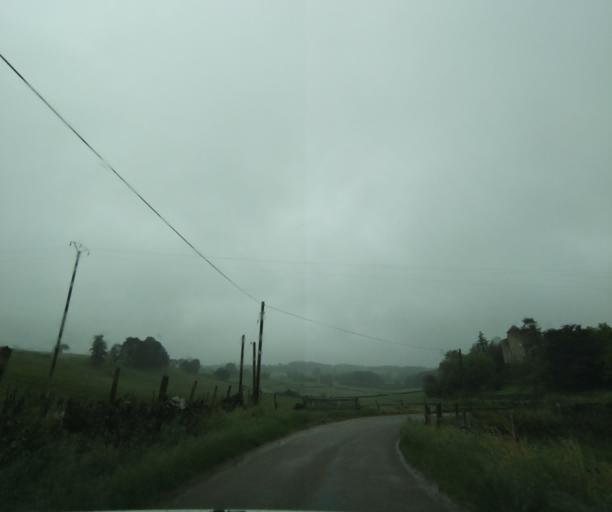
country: FR
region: Bourgogne
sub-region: Departement de Saone-et-Loire
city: Charolles
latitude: 46.3936
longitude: 4.2928
